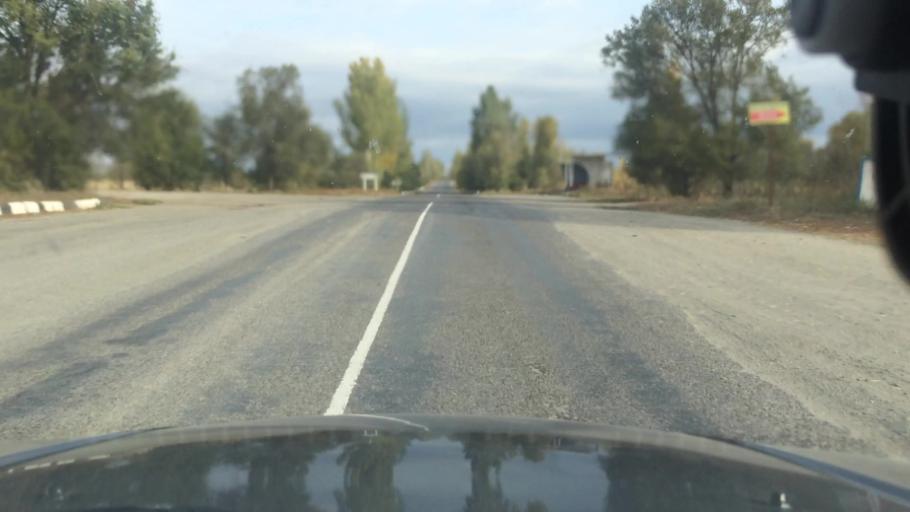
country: KG
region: Ysyk-Koel
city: Karakol
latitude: 42.5645
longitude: 78.3914
